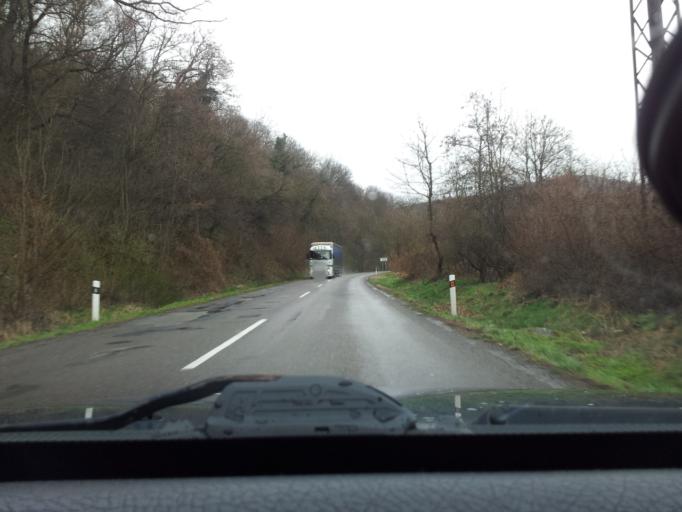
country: SK
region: Nitriansky
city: Tlmace
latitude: 48.3402
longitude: 18.5577
